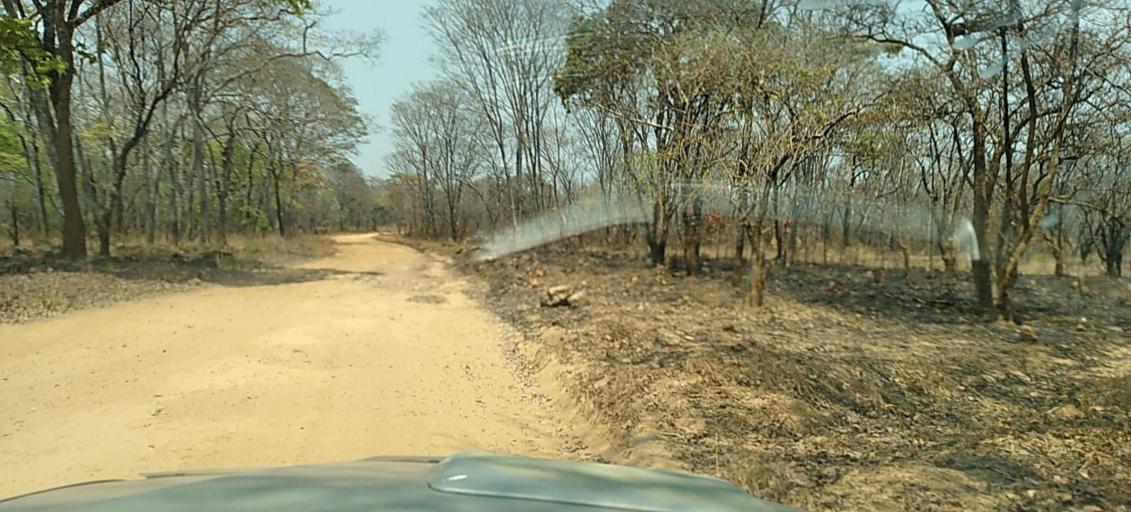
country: ZM
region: North-Western
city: Kasempa
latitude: -13.6166
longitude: 26.2007
